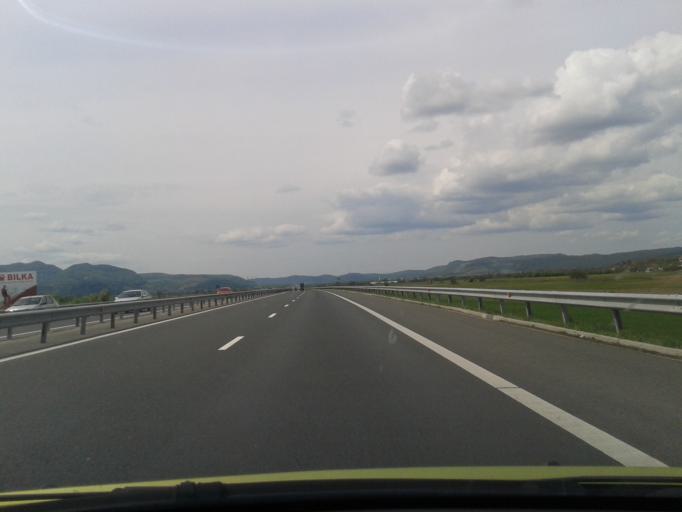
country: RO
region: Hunedoara
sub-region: Comuna Harau
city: Harau
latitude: 45.8875
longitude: 22.9761
